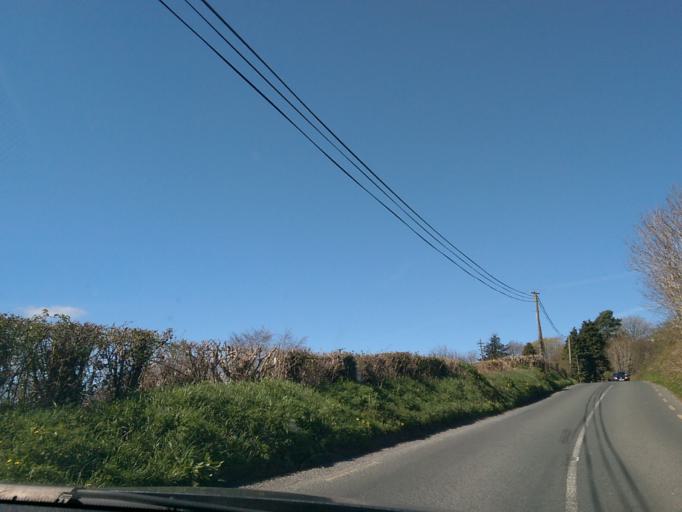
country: IE
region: Leinster
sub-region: Wicklow
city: Baltinglass
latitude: 52.8762
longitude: -6.5780
